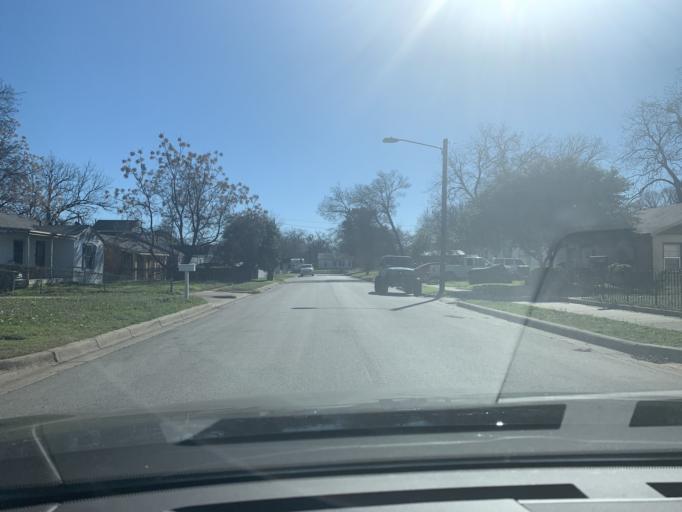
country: US
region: Texas
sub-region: Tarrant County
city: Haltom City
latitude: 32.7663
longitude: -97.2902
